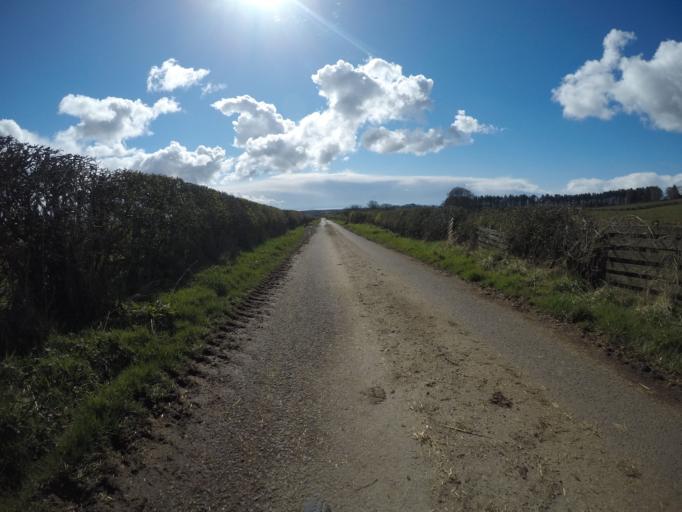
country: GB
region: Scotland
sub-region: North Ayrshire
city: Dalry
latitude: 55.6800
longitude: -4.7258
